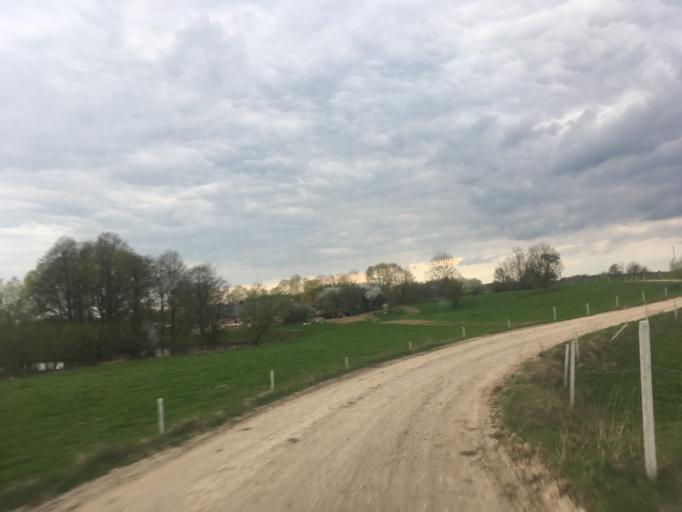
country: PL
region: Podlasie
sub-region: Powiat sejnenski
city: Punsk
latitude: 54.2865
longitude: 23.1029
